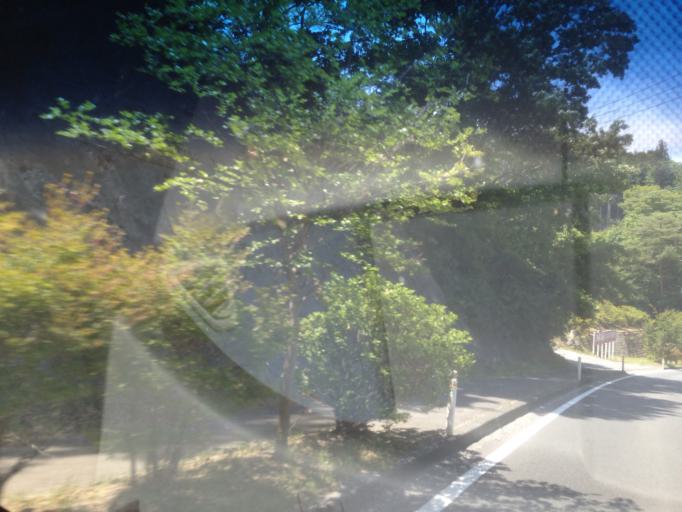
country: JP
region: Iwate
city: Kamaishi
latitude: 39.3166
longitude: 141.8839
